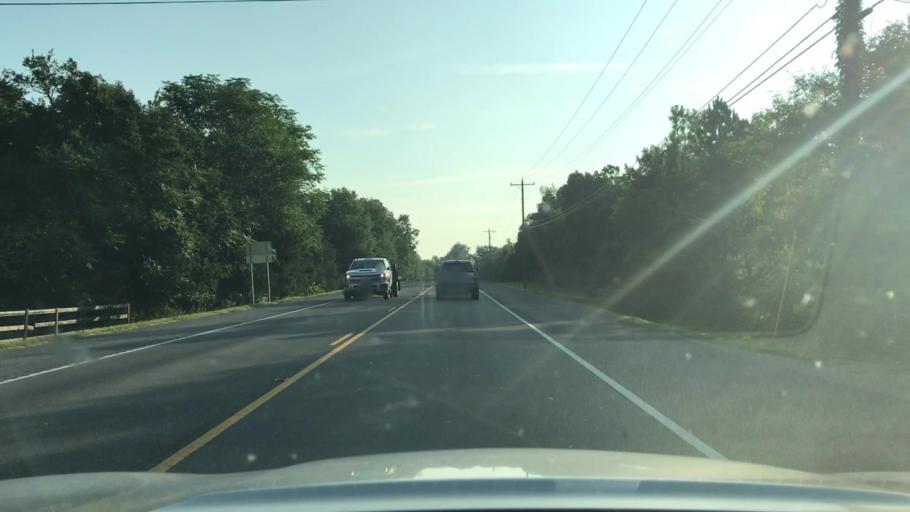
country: US
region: Tennessee
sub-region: Rutherford County
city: La Vergne
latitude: 36.0653
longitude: -86.5900
